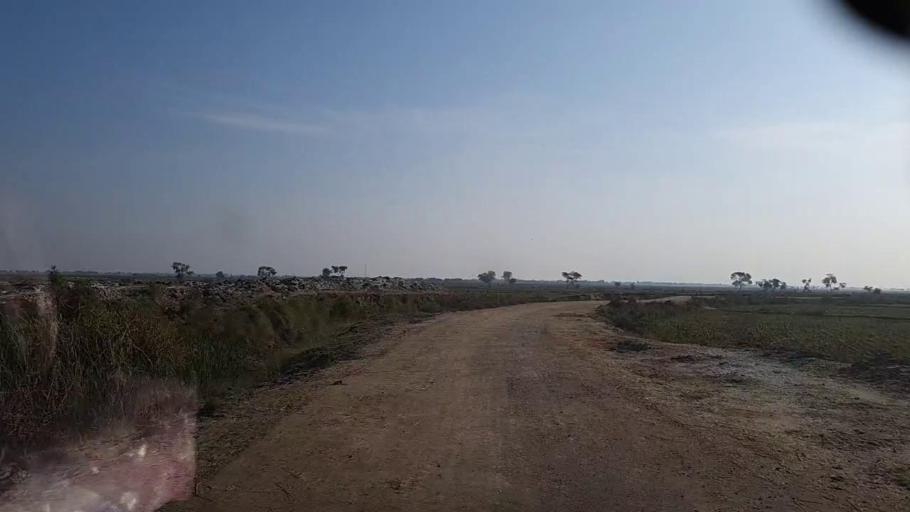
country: PK
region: Sindh
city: Jacobabad
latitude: 28.2950
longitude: 68.5583
